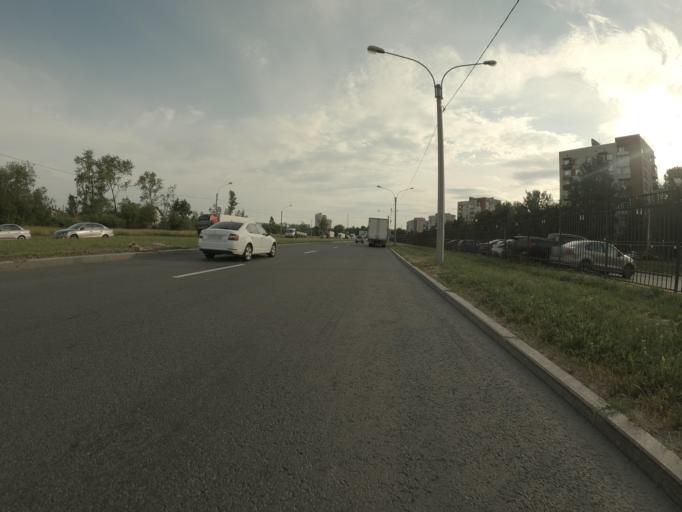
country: RU
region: Leningrad
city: Rybatskoye
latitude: 59.8807
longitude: 30.4857
